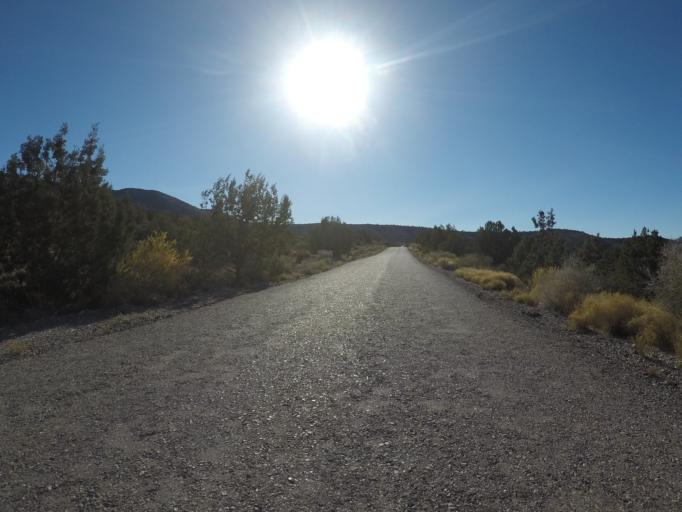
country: US
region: Nevada
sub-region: Clark County
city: Summerlin South
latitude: 36.0943
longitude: -115.5648
